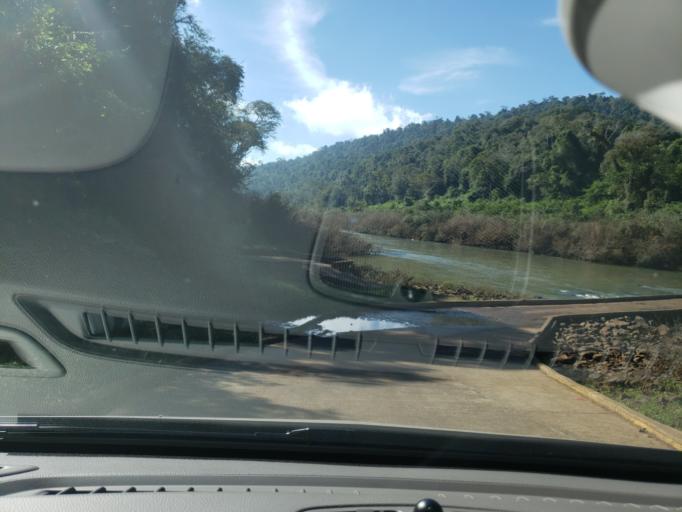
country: BR
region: Rio Grande do Sul
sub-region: Tres Passos
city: Tres Passos
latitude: -27.1449
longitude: -53.9080
